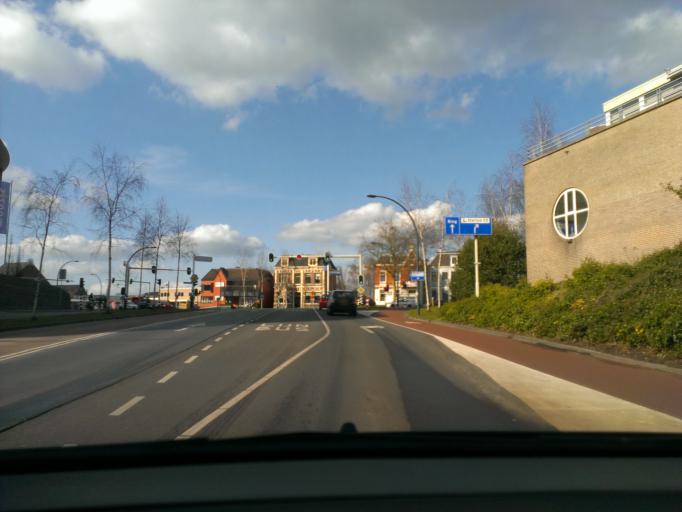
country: NL
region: Overijssel
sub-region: Gemeente Enschede
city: Enschede
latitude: 52.2223
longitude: 6.8873
